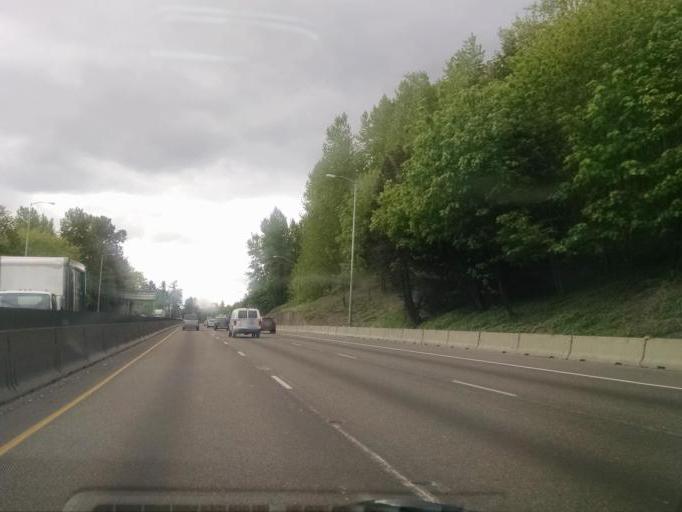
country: US
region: Oregon
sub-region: Multnomah County
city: Portland
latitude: 45.4849
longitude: -122.6793
